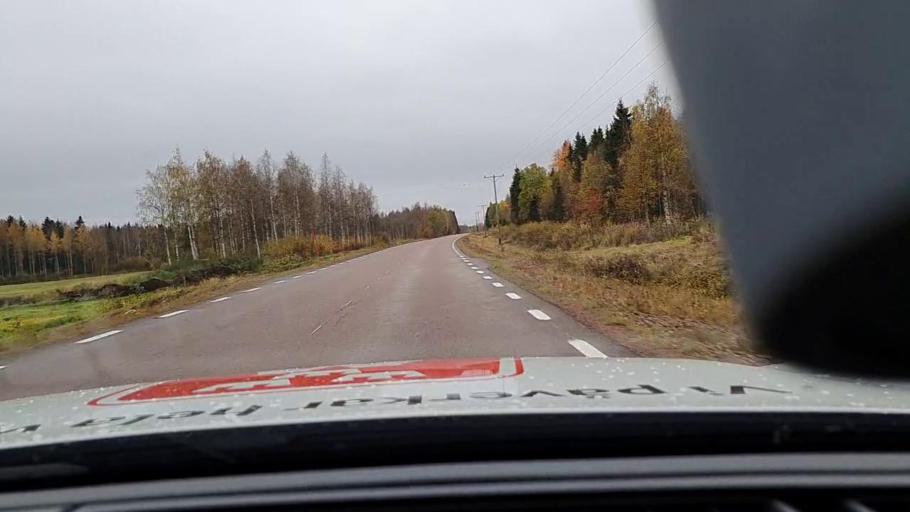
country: FI
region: Lapland
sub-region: Torniolaakso
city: Ylitornio
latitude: 66.1279
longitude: 23.9105
